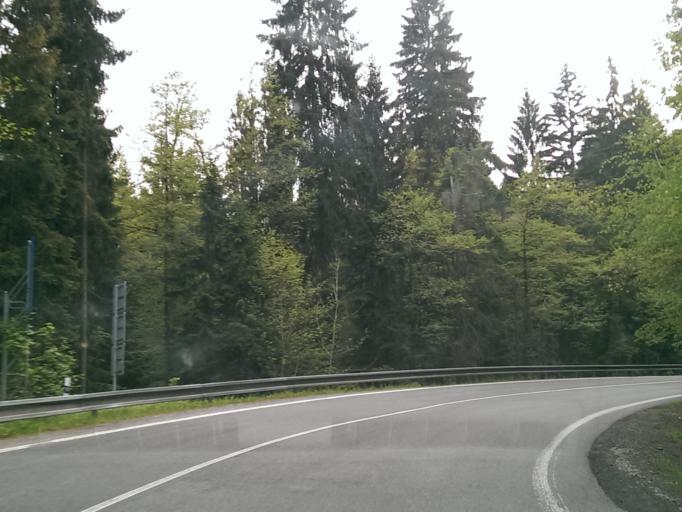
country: CZ
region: Liberecky
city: Zelezny Brod
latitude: 50.6693
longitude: 15.2643
